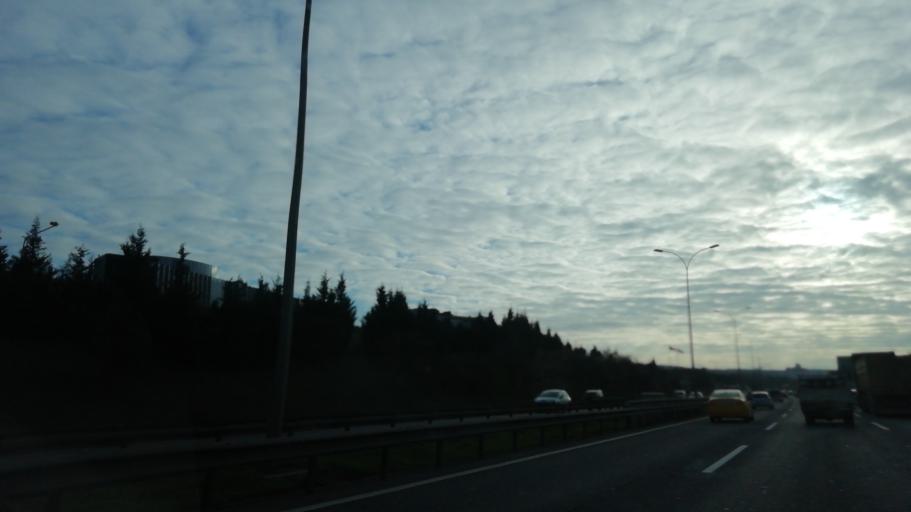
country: TR
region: Kocaeli
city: Balcik
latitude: 40.8790
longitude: 29.3836
